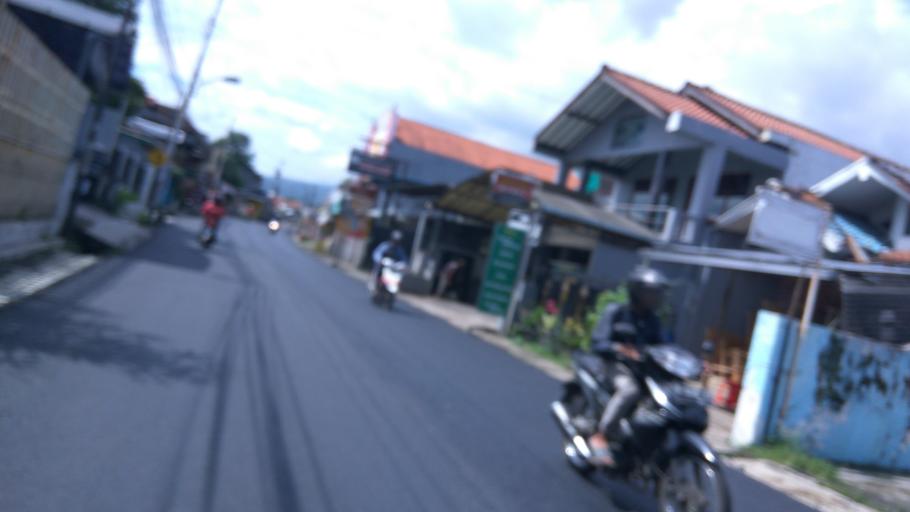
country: ID
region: Central Java
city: Ungaran
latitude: -7.1242
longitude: 110.4094
